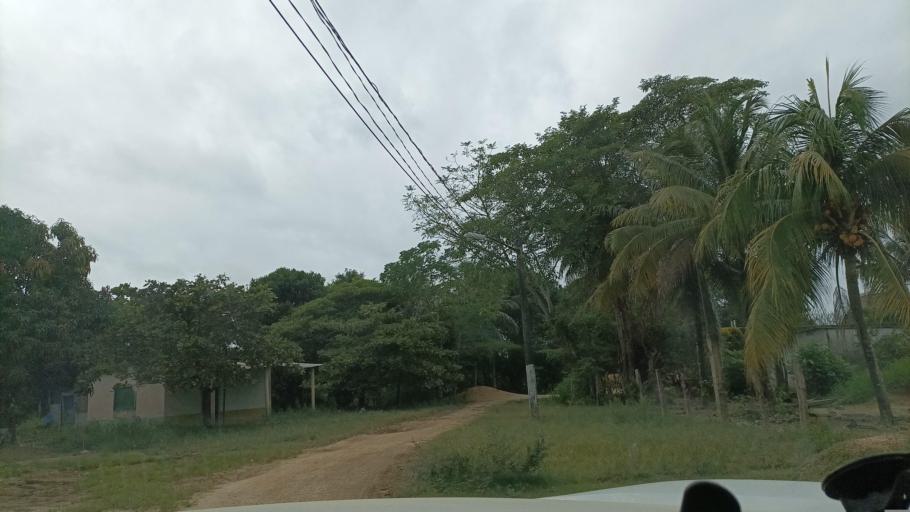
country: MX
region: Veracruz
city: Hidalgotitlan
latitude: 17.8116
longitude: -94.5419
